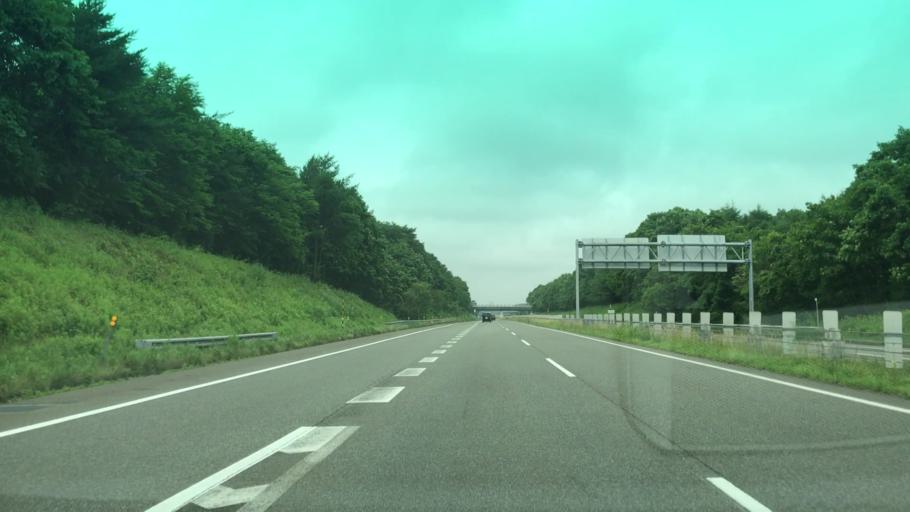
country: JP
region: Hokkaido
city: Tomakomai
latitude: 42.7129
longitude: 141.6522
